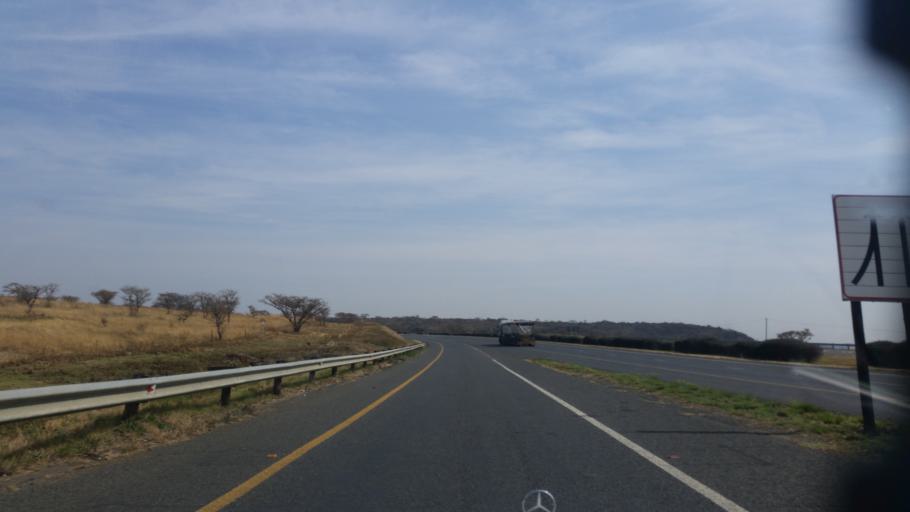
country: ZA
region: KwaZulu-Natal
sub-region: uThukela District Municipality
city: Estcourt
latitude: -29.0473
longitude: 29.8890
